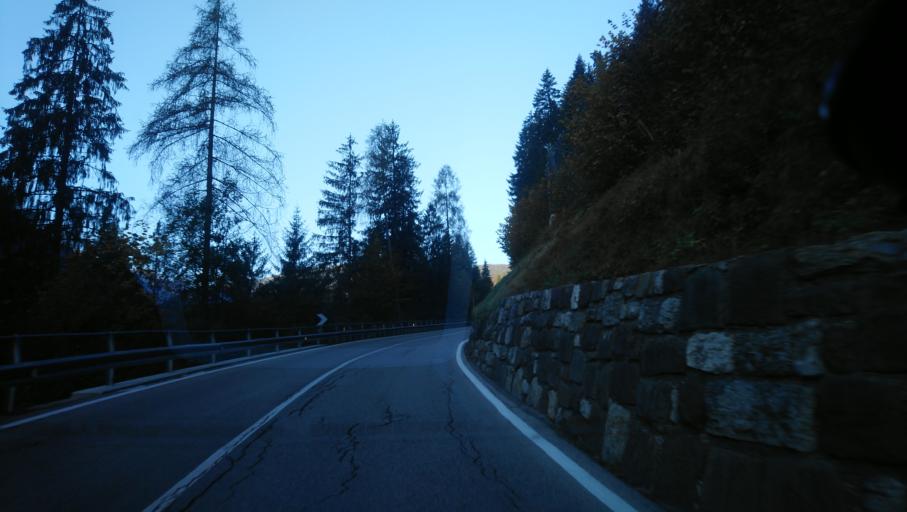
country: IT
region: Veneto
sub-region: Provincia di Belluno
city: Canale d'Agordo
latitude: 46.3633
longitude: 11.9071
